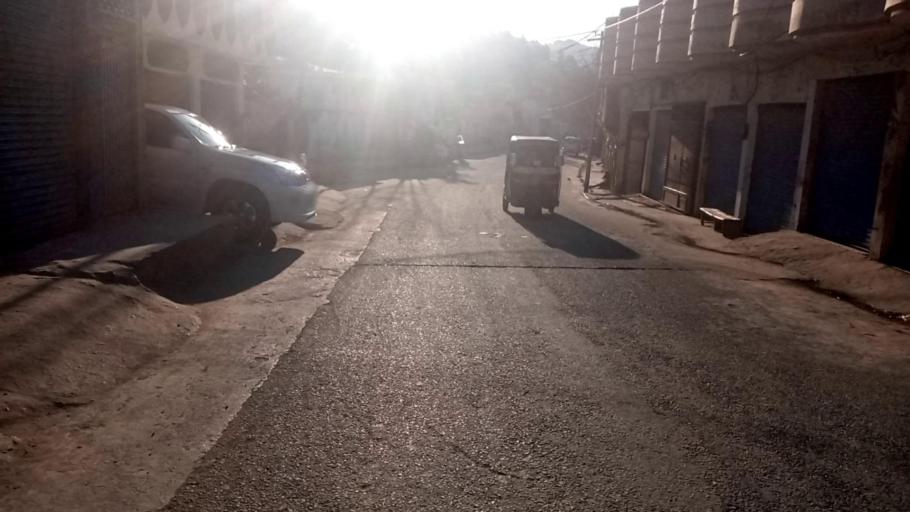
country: PK
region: Khyber Pakhtunkhwa
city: Saidu Sharif
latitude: 34.7435
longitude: 72.3558
